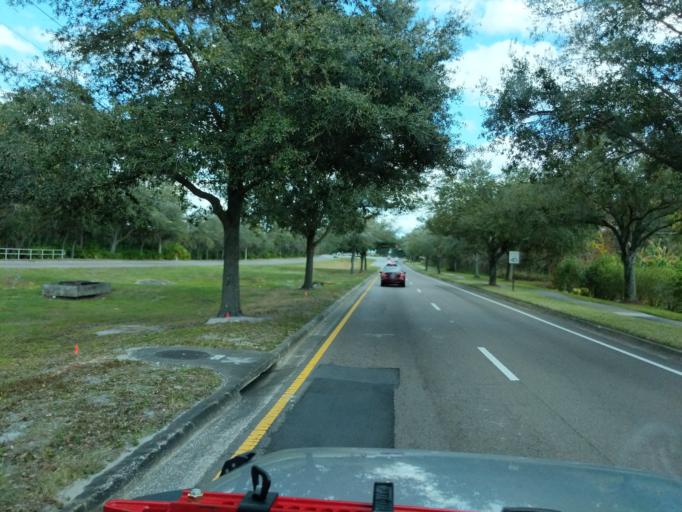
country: US
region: Florida
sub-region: Seminole County
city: Oviedo
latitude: 28.6558
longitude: -81.1876
